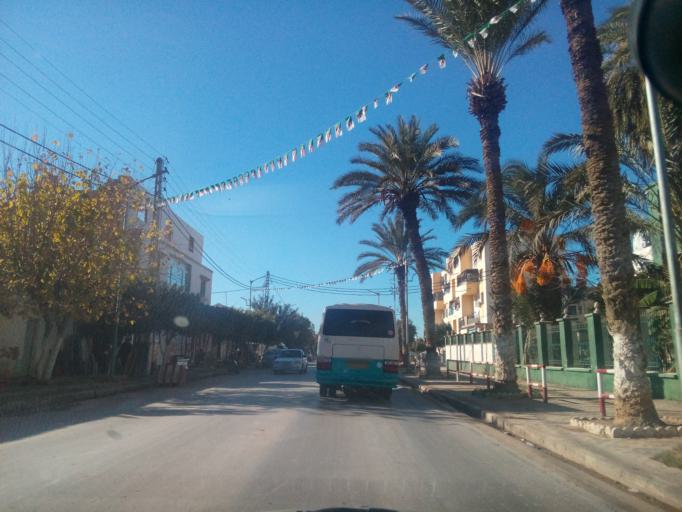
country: DZ
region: Relizane
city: Djidiouia
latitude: 35.9296
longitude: 0.8326
